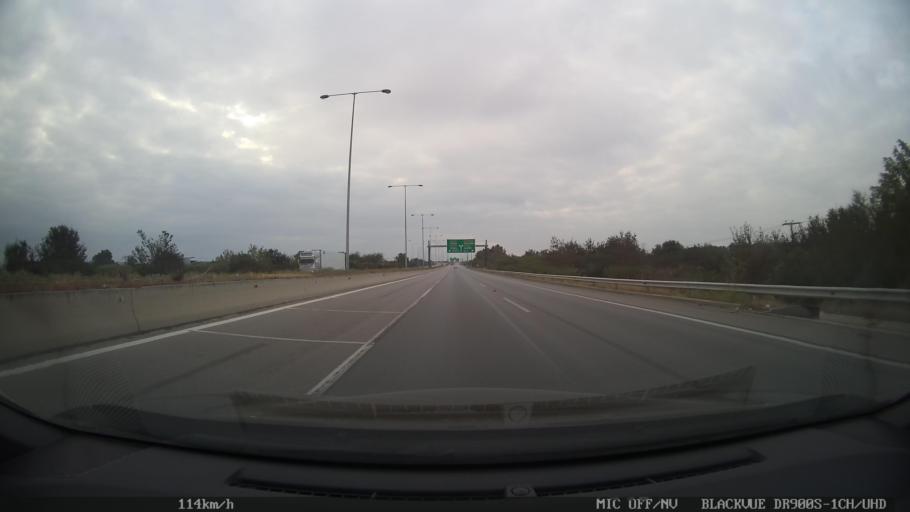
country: GR
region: Central Macedonia
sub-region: Nomos Thessalonikis
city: Nea Magnisia
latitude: 40.6632
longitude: 22.8375
